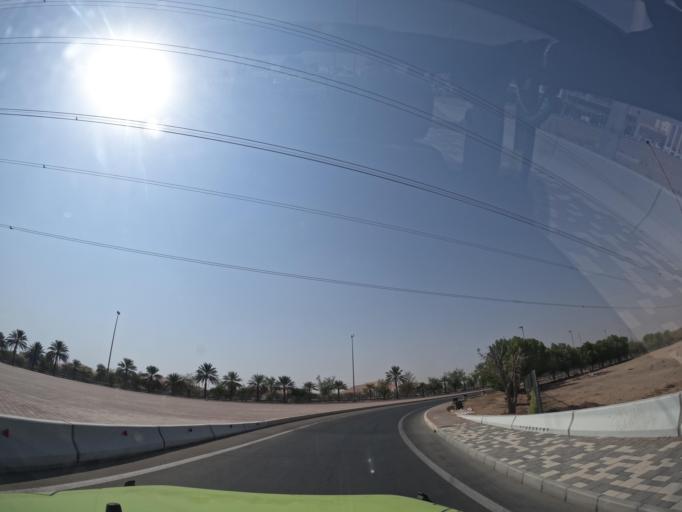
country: AE
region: Abu Dhabi
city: Al Ain
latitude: 24.2234
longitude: 55.5535
